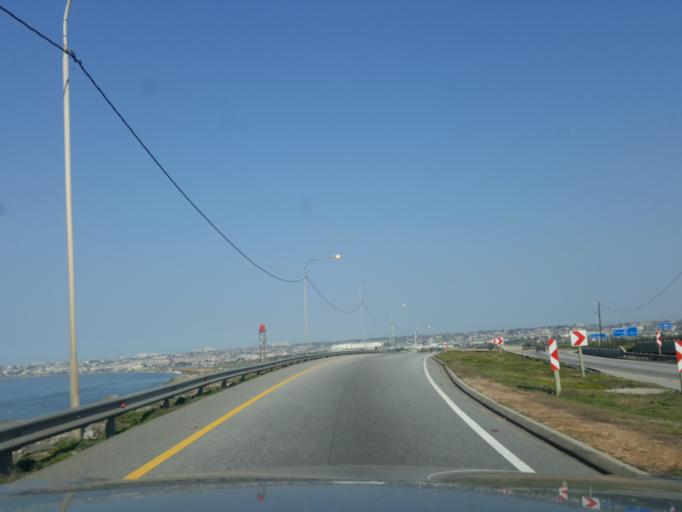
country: ZA
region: Eastern Cape
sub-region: Nelson Mandela Bay Metropolitan Municipality
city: Port Elizabeth
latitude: -33.9128
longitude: 25.6155
